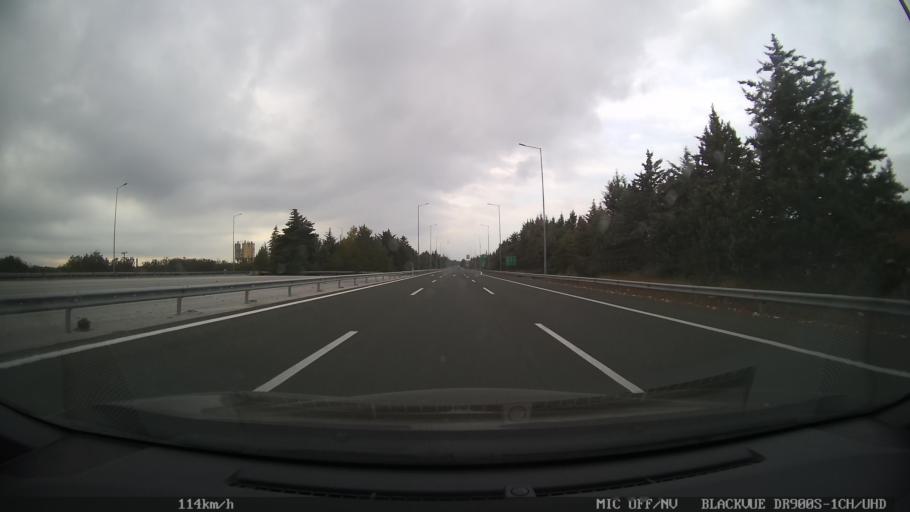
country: GR
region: Central Macedonia
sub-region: Nomos Pierias
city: Korinos
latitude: 40.3361
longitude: 22.5854
